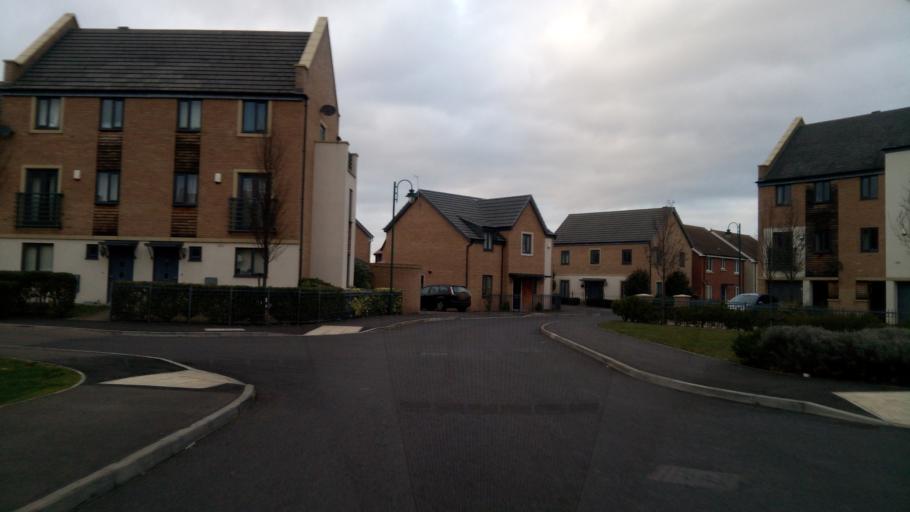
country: GB
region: England
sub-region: Cambridgeshire
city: Yaxley
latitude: 52.5306
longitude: -0.2835
